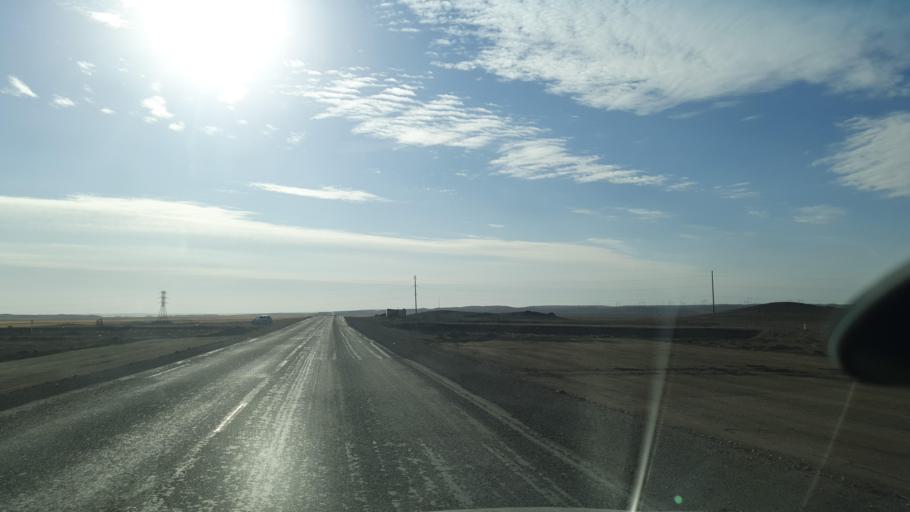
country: KZ
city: Priozersk
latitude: 45.8492
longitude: 73.4621
